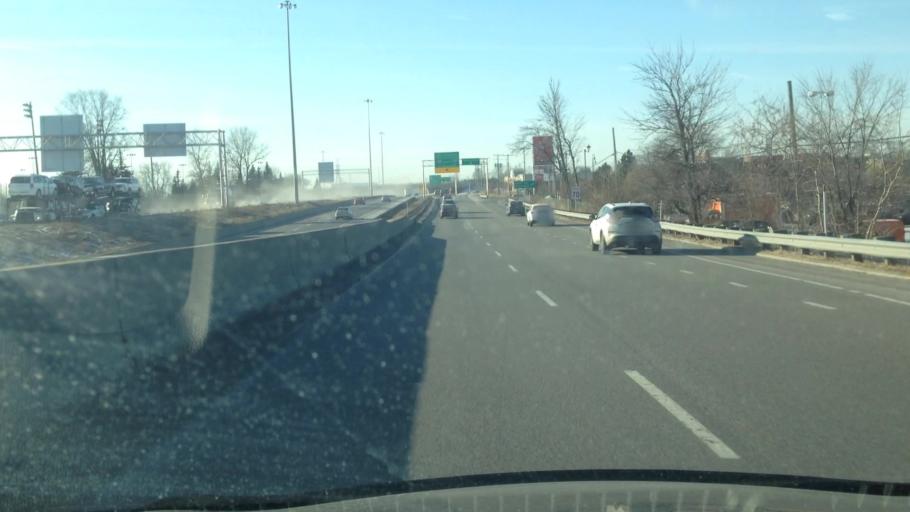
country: CA
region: Quebec
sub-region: Laurentides
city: Boisbriand
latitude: 45.6251
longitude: -73.8442
